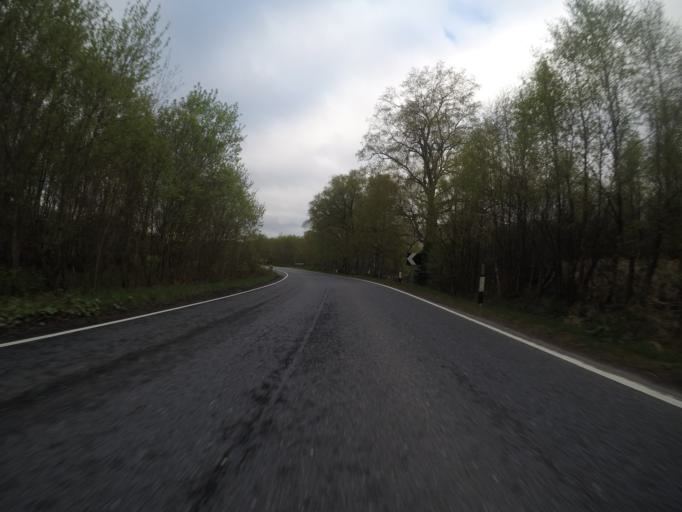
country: GB
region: Scotland
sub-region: Highland
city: Spean Bridge
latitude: 56.9530
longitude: -4.4930
